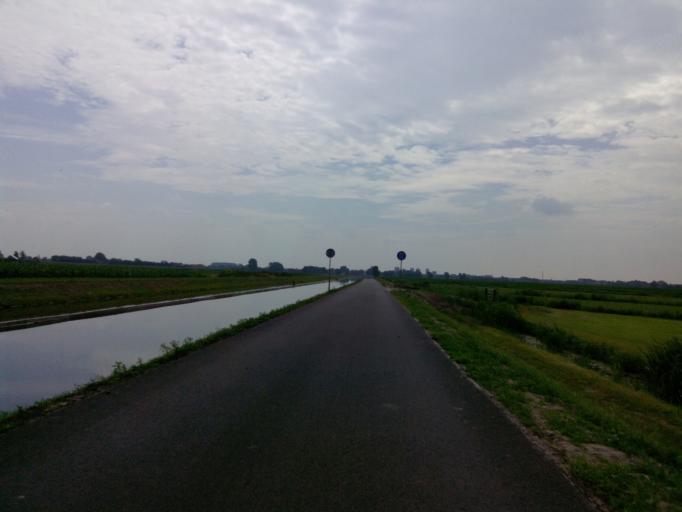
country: NL
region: Utrecht
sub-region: Gemeente Bunschoten
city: Bunschoten
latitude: 52.2183
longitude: 5.3972
